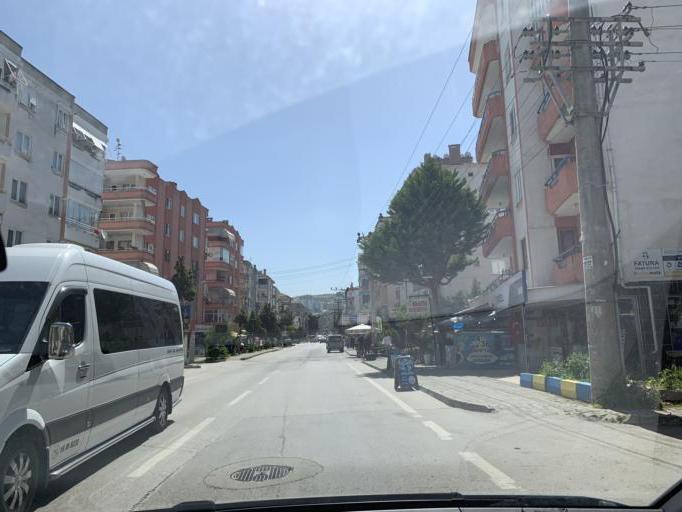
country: TR
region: Bursa
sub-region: Mudanya
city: Mudanya
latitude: 40.3562
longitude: 28.9210
